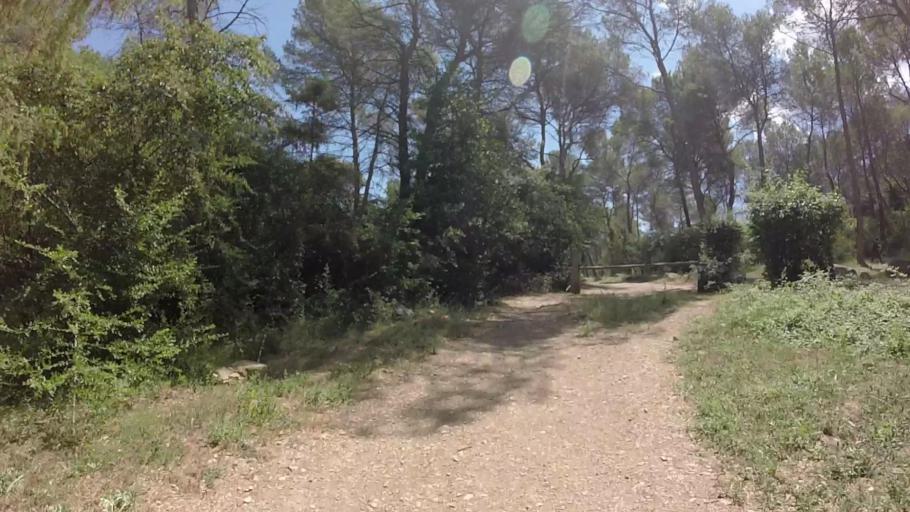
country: FR
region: Provence-Alpes-Cote d'Azur
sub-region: Departement des Alpes-Maritimes
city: Mougins
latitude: 43.5980
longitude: 7.0167
